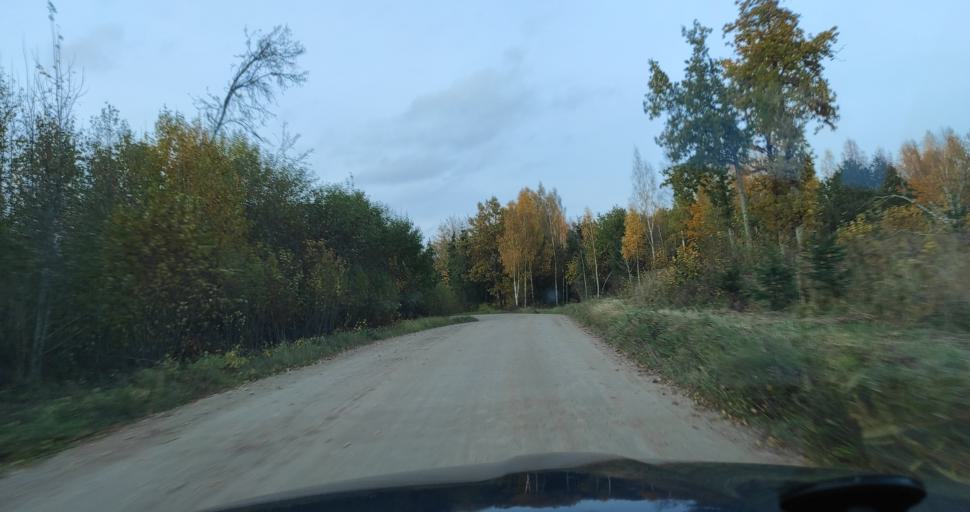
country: LV
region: Vainode
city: Vainode
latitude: 56.6349
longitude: 21.8124
